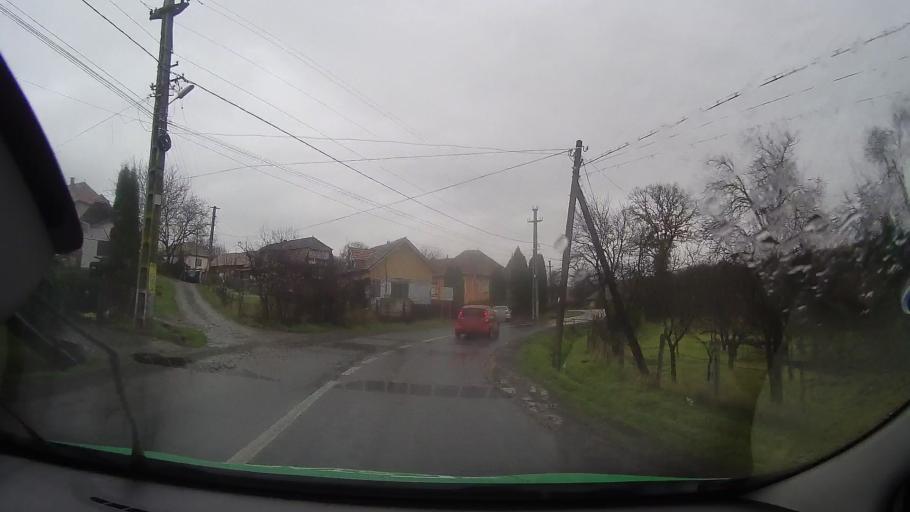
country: RO
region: Mures
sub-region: Comuna Vatava
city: Vatava
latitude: 46.9465
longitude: 24.7619
